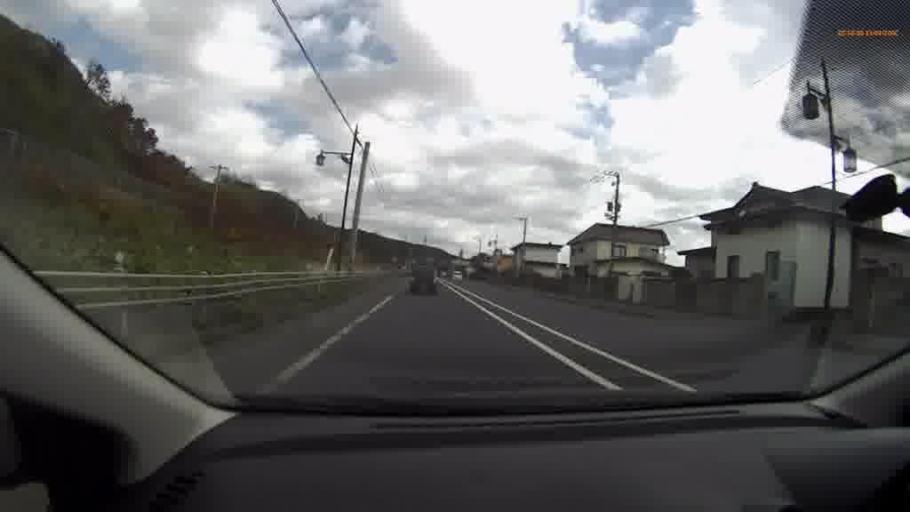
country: JP
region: Hokkaido
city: Kushiro
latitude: 42.9538
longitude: 144.0914
